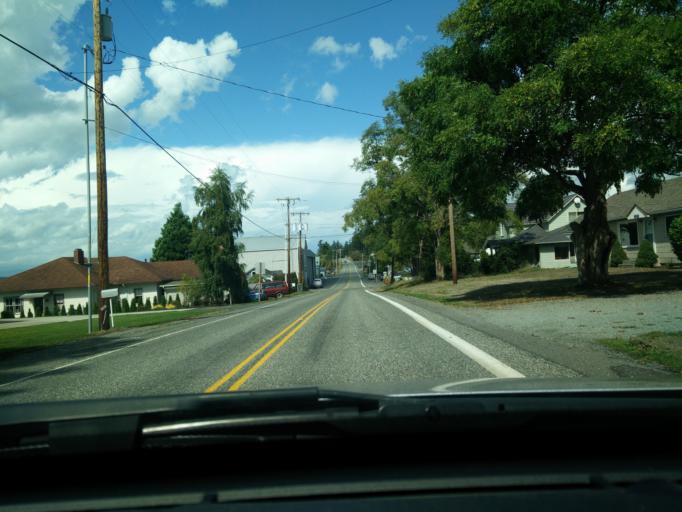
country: US
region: Washington
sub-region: Skagit County
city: Anacortes
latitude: 48.4829
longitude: -122.4774
